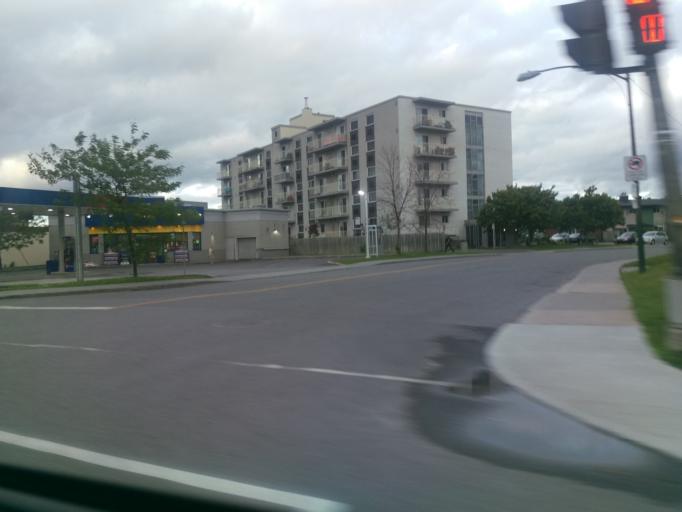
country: CA
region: Quebec
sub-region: Outaouais
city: Gatineau
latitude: 45.4595
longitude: -75.7415
